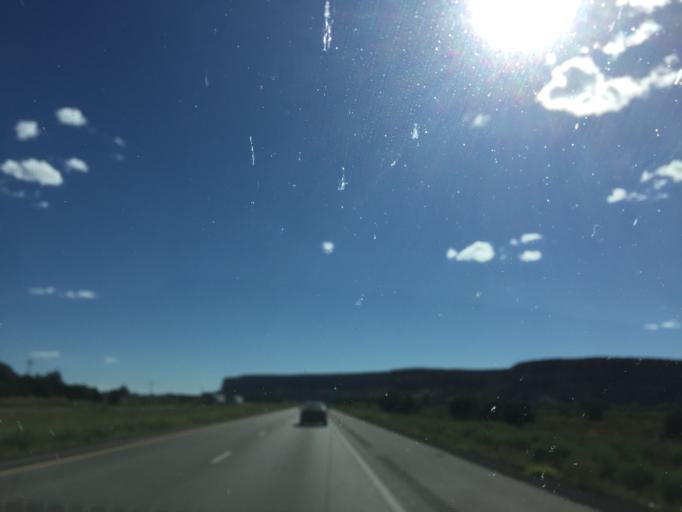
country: US
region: Arizona
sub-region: Apache County
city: Houck
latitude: 35.3808
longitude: -109.0206
